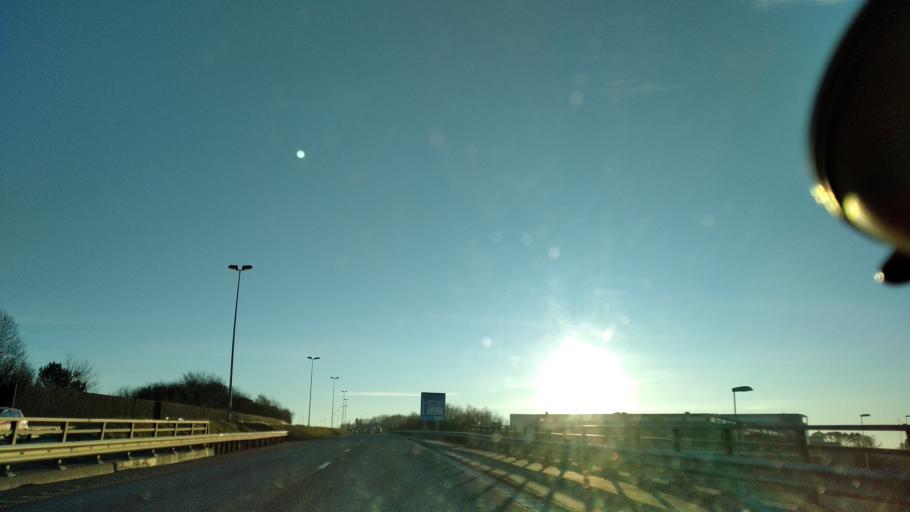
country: NO
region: Rogaland
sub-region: Sandnes
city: Sandnes
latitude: 58.8628
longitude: 5.7113
